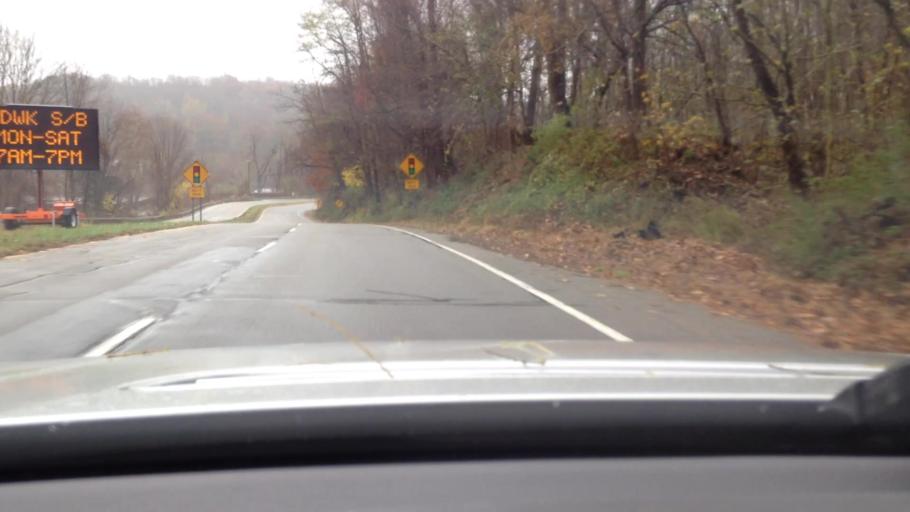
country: US
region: New York
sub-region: Westchester County
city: Peekskill
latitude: 41.3082
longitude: -73.9312
